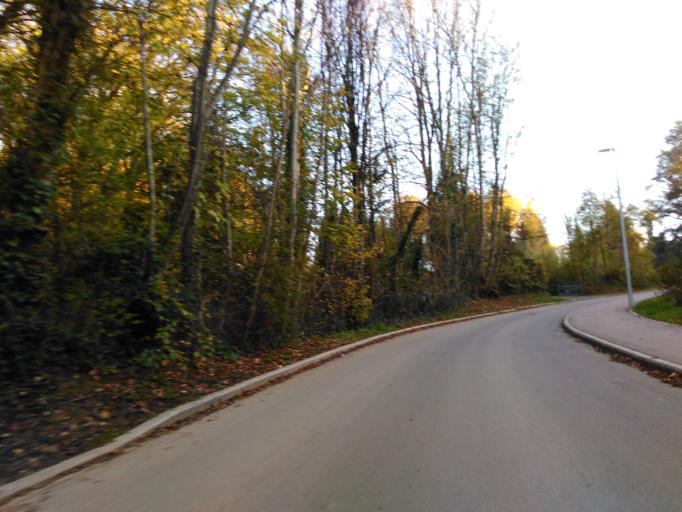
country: LU
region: Luxembourg
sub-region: Canton d'Esch-sur-Alzette
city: Esch-sur-Alzette
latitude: 49.4884
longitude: 5.9856
